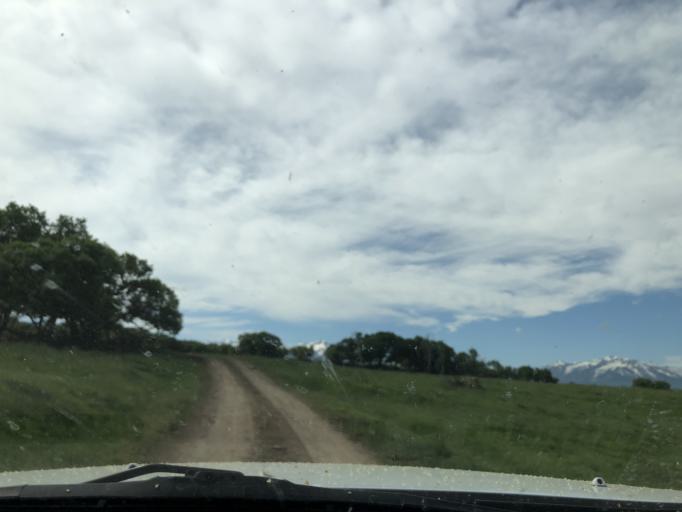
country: US
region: Colorado
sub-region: Delta County
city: Paonia
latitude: 39.0204
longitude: -107.3432
